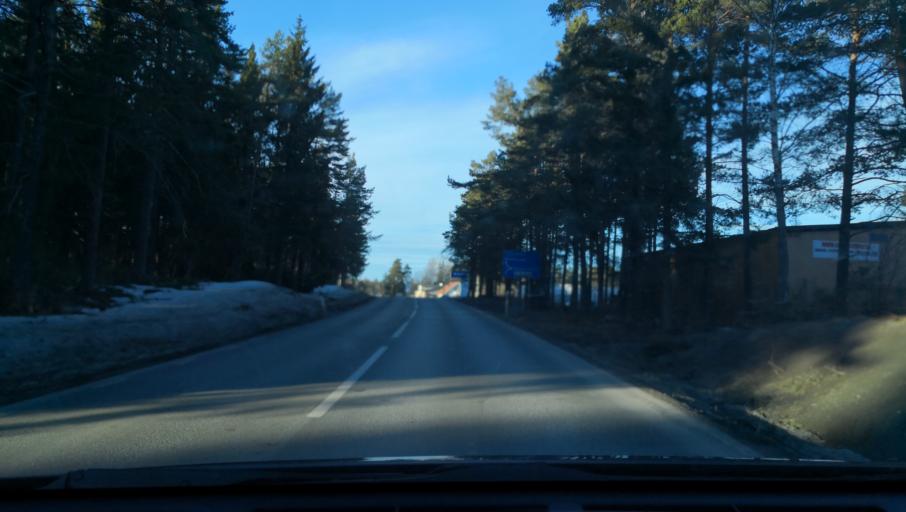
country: SE
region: Uppsala
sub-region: Osthammars Kommun
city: OEsthammar
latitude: 60.2518
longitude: 18.3475
